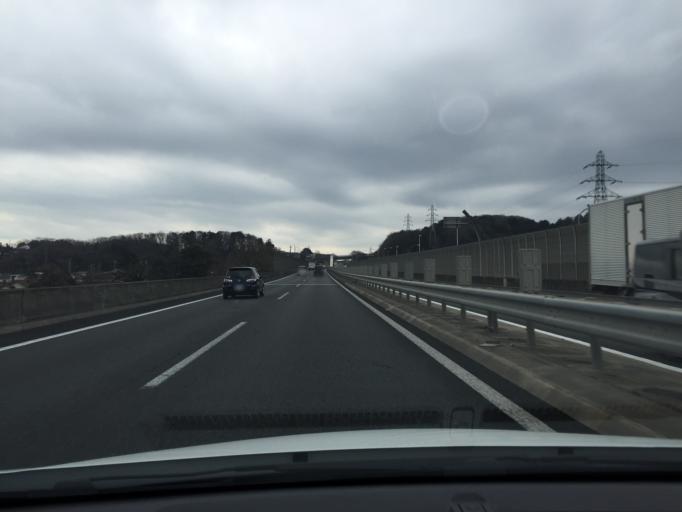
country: JP
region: Saitama
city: Sayama
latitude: 35.8412
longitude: 139.3691
